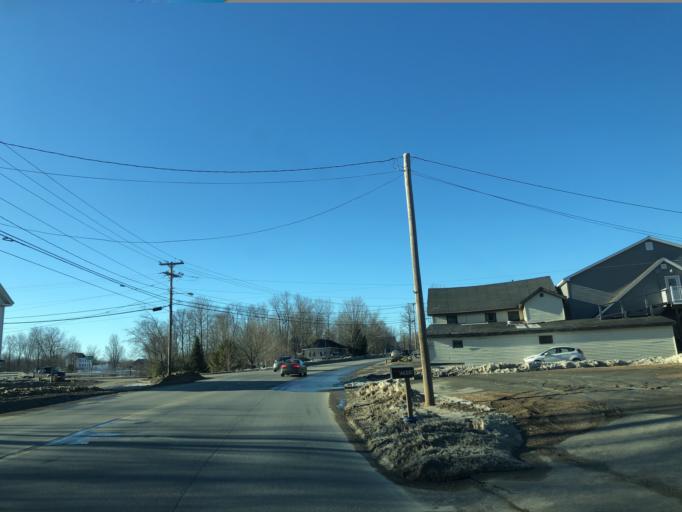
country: US
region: Maine
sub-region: Penobscot County
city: Kenduskeag
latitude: 44.9190
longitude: -68.9304
